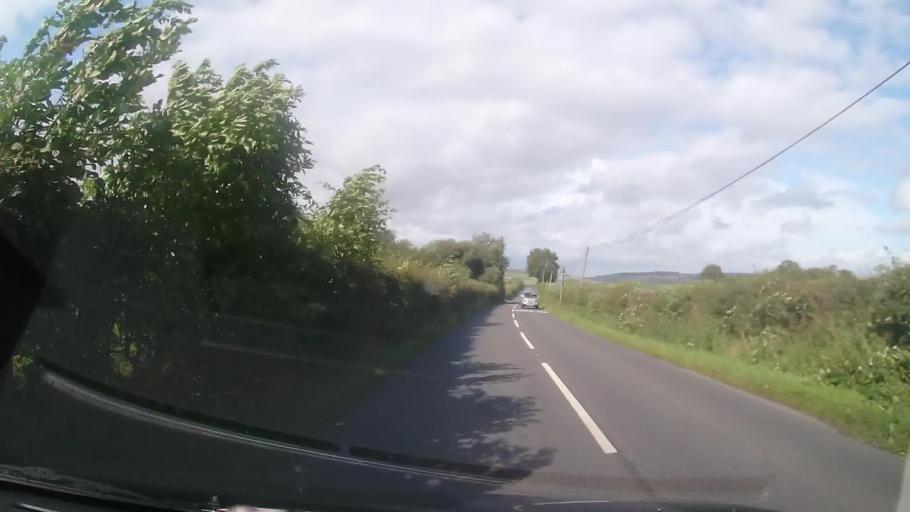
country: GB
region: Wales
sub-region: Sir Powys
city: Knighton
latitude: 52.3721
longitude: -3.0504
